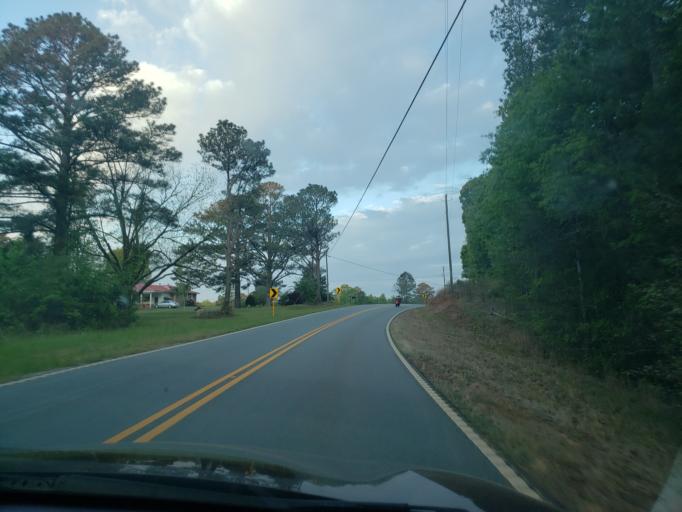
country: US
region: Alabama
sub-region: Tallapoosa County
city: Dadeville
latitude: 32.7023
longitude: -85.7554
